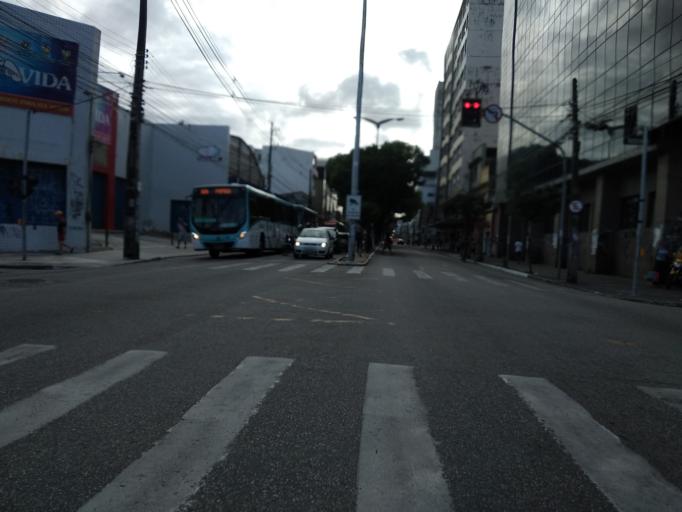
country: BR
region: Ceara
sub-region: Fortaleza
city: Fortaleza
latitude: -3.7325
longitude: -38.5276
